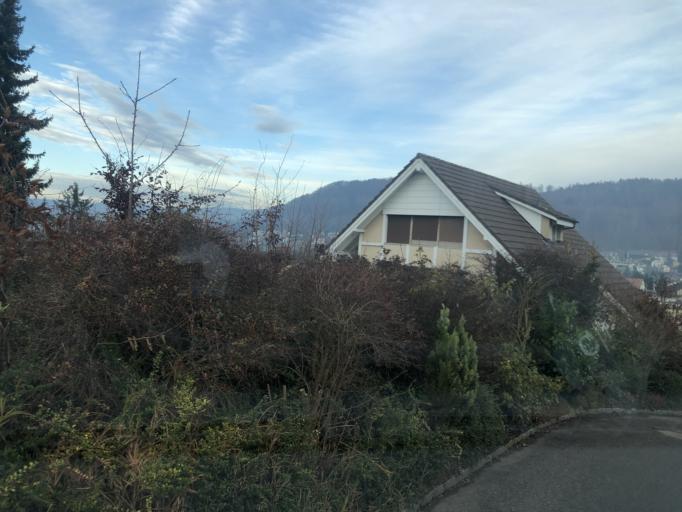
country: CH
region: Aargau
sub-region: Bezirk Baden
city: Gebenstorf
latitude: 47.4773
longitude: 8.2389
